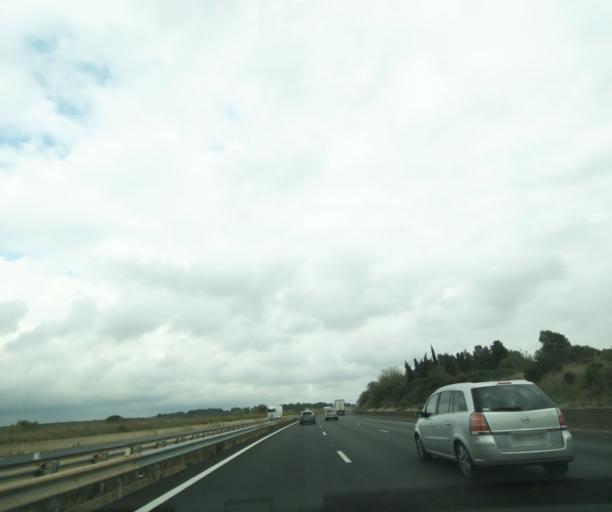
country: FR
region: Languedoc-Roussillon
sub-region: Departement de l'Herault
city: Loupian
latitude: 43.4576
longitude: 3.6111
